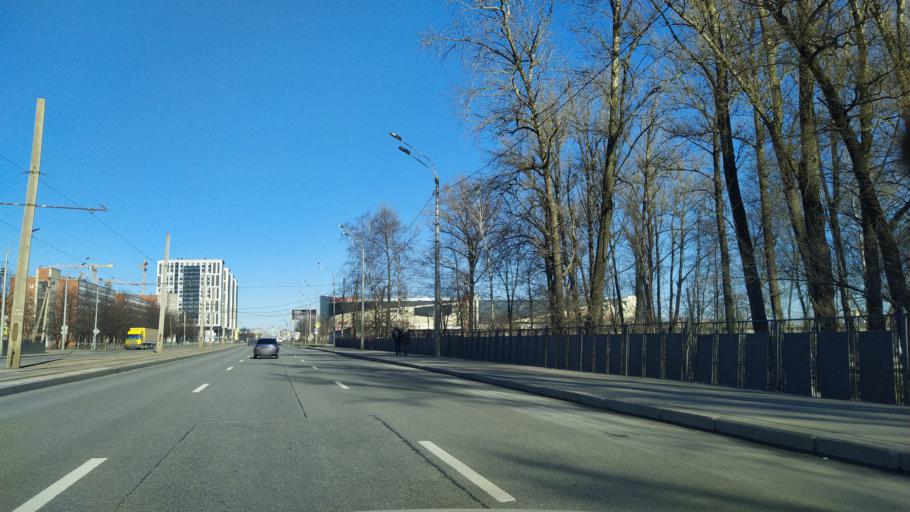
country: RU
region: St.-Petersburg
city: Kupchino
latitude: 59.8815
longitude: 30.3614
